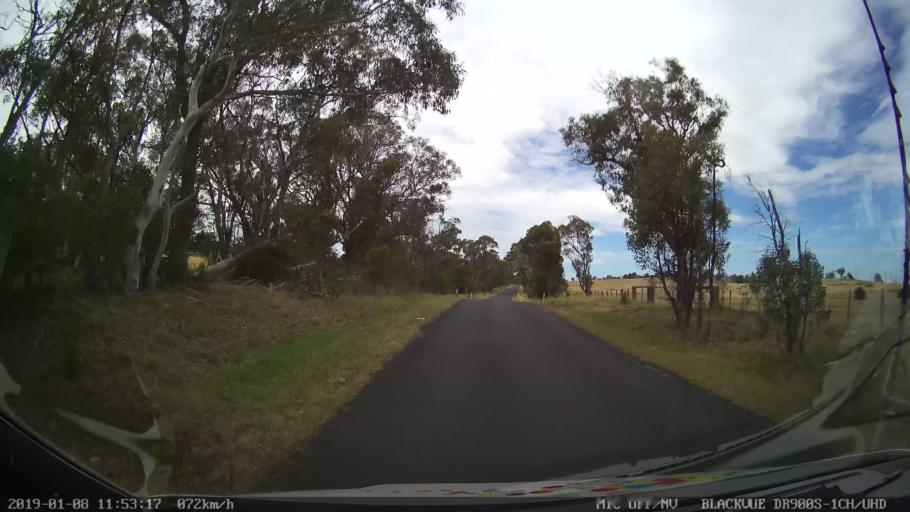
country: AU
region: New South Wales
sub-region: Armidale Dumaresq
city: Armidale
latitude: -30.4128
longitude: 151.5605
